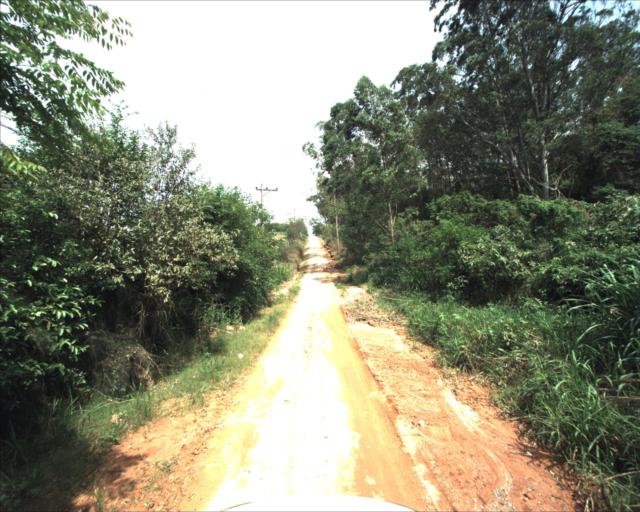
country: BR
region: Sao Paulo
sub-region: Salto De Pirapora
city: Salto de Pirapora
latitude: -23.5667
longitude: -47.5391
